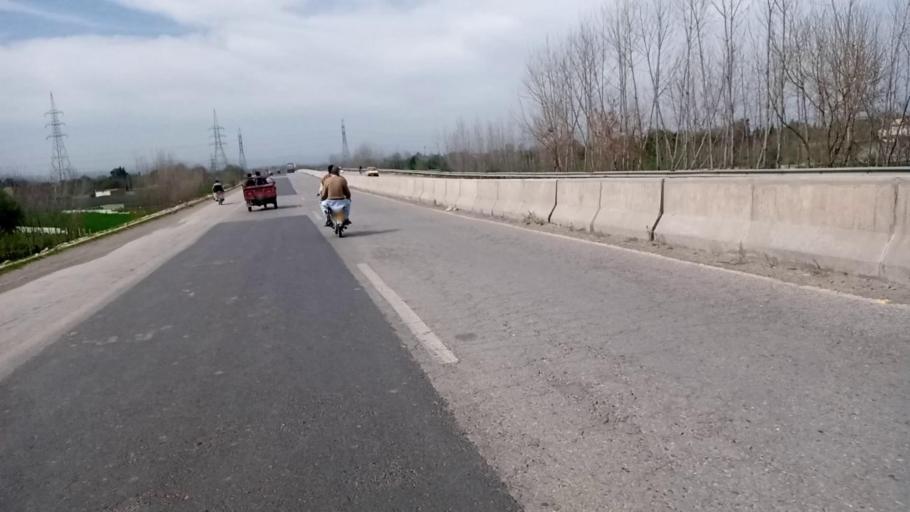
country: PK
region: Khyber Pakhtunkhwa
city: Peshawar
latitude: 34.0613
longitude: 71.6057
